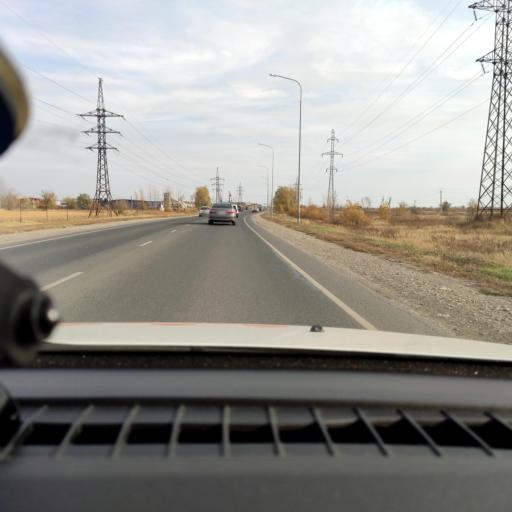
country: RU
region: Samara
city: Samara
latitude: 53.1311
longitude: 50.1448
